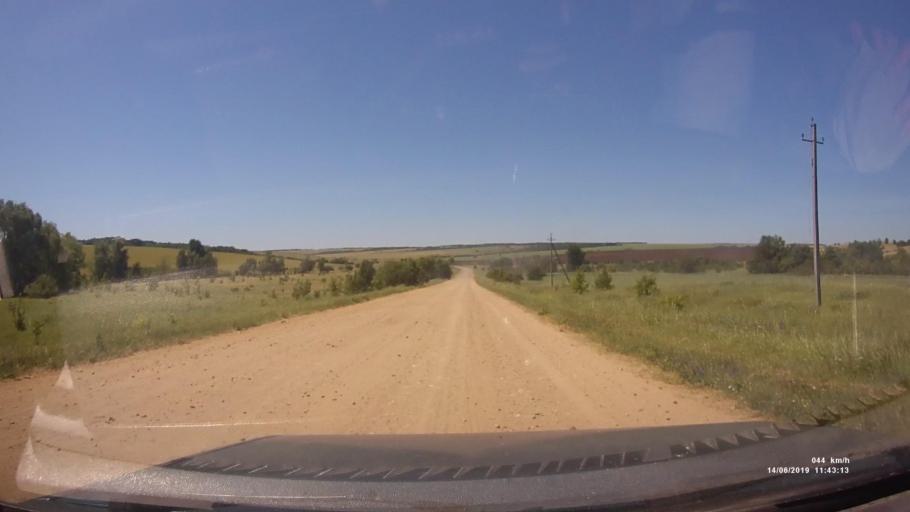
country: RU
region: Rostov
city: Kazanskaya
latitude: 49.8579
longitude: 41.3360
